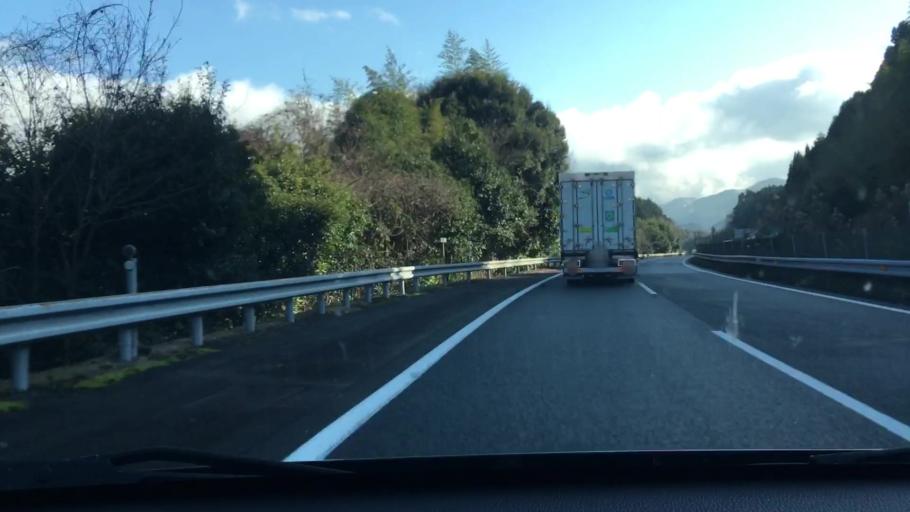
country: JP
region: Kumamoto
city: Hitoyoshi
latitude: 32.1687
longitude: 130.7927
